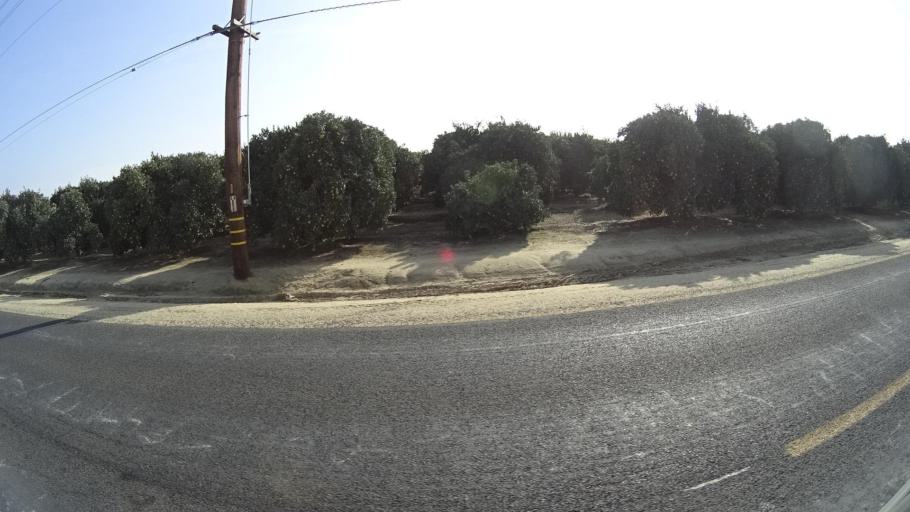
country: US
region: California
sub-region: Tulare County
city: Richgrove
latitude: 35.7760
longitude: -119.1622
